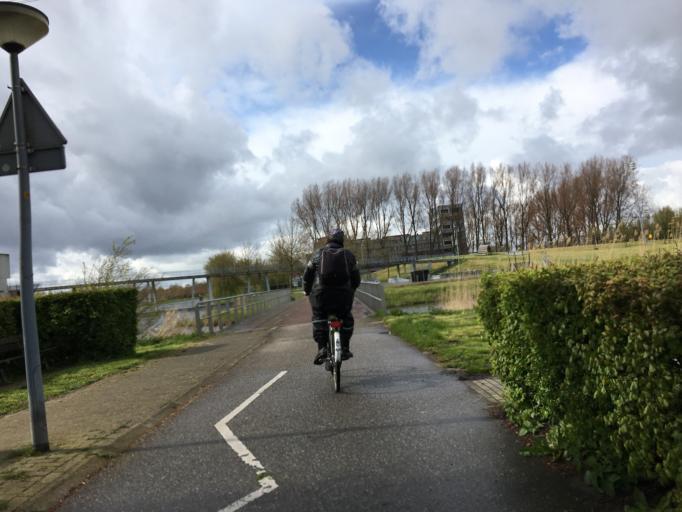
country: NL
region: Flevoland
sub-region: Gemeente Almere
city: Almere Stad
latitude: 52.3733
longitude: 5.2567
